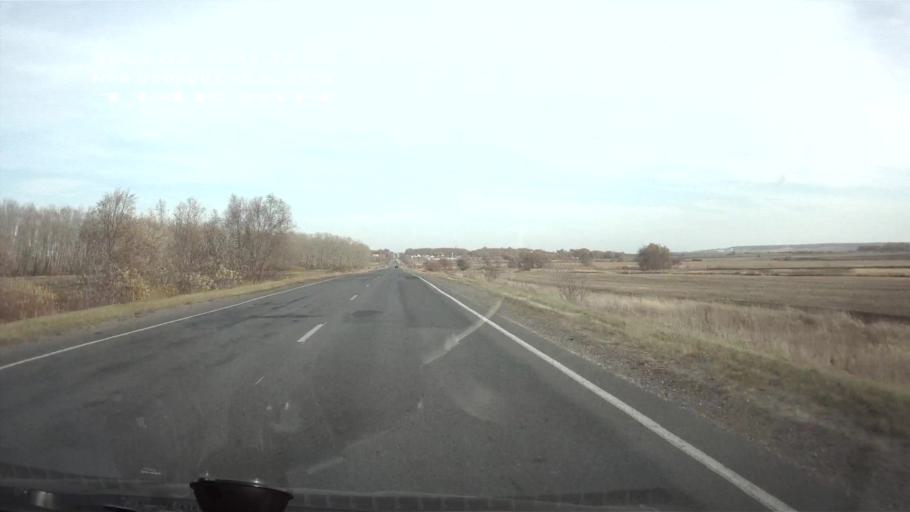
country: RU
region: Mordoviya
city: Atyashevo
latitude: 54.5507
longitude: 45.9560
